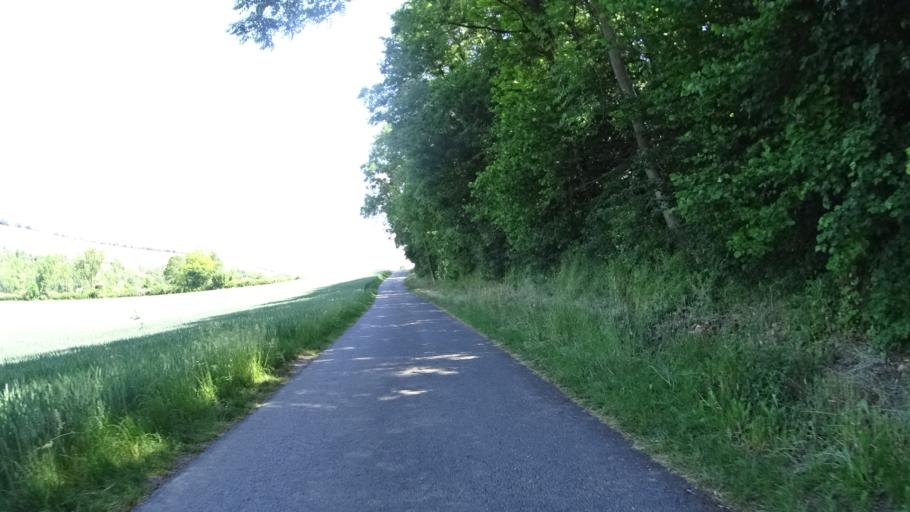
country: DE
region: Bavaria
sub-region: Regierungsbezirk Unterfranken
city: Tauberrettersheim
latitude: 49.4954
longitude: 9.9519
